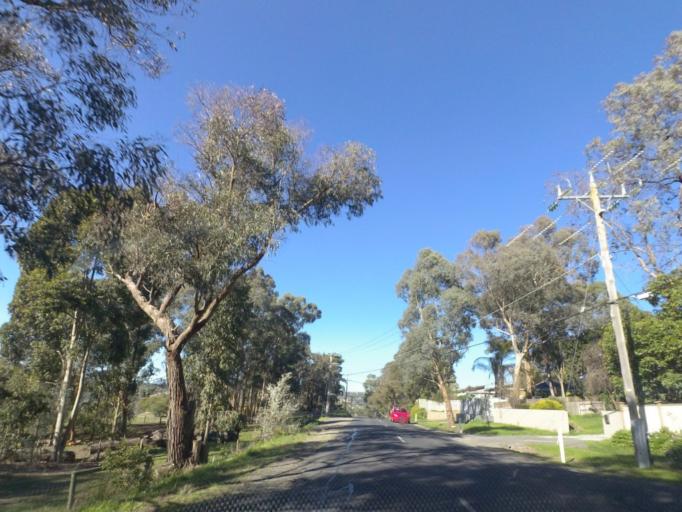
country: AU
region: Victoria
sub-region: Maroondah
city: Croydon North
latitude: -37.7625
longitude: 145.2857
